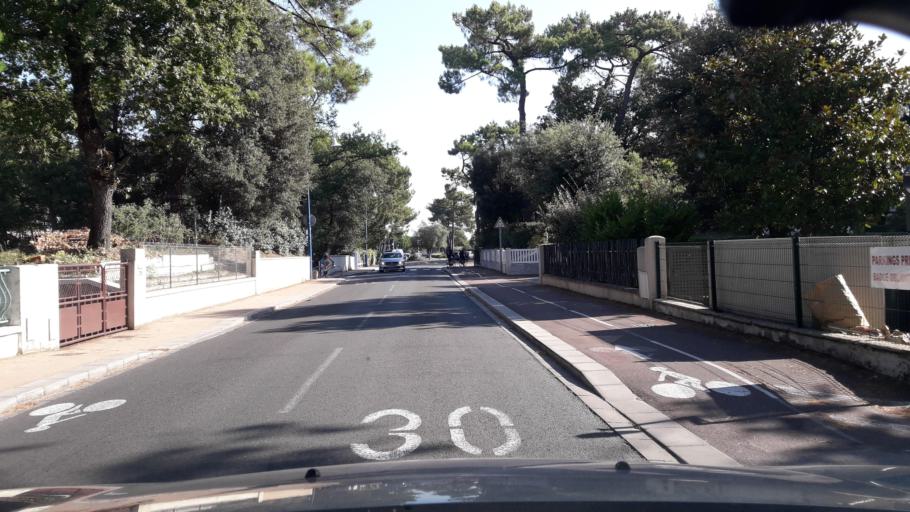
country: FR
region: Poitou-Charentes
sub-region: Departement de la Charente-Maritime
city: Les Mathes
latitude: 45.6933
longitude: -1.1785
